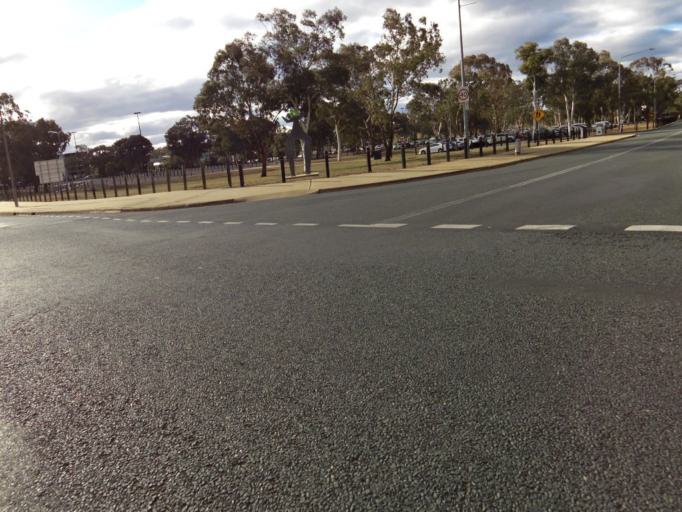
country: AU
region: Australian Capital Territory
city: Kaleen
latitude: -35.2482
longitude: 149.0998
